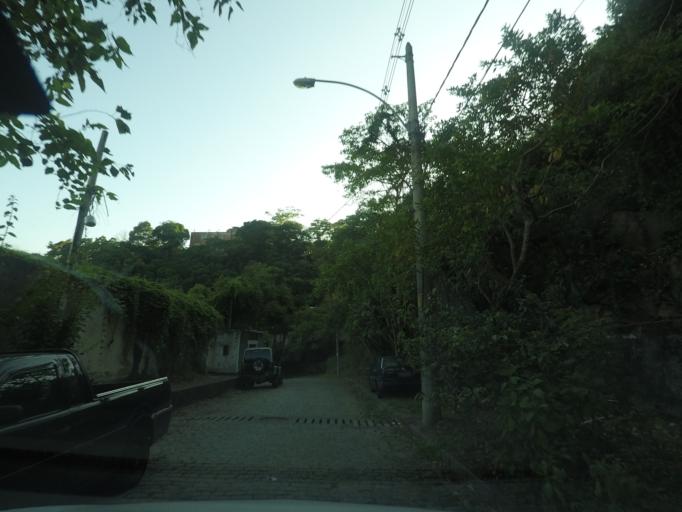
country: BR
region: Rio de Janeiro
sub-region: Rio De Janeiro
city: Rio de Janeiro
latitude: -22.9441
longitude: -43.1907
